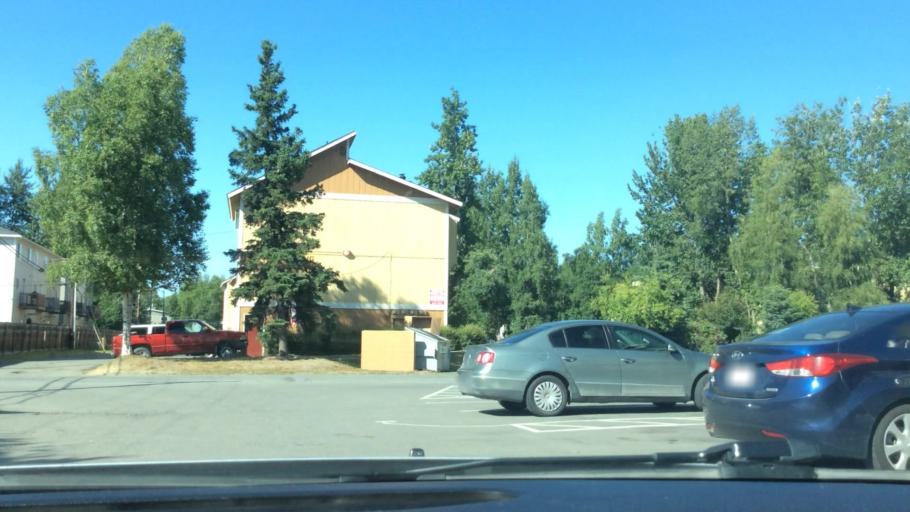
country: US
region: Alaska
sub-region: Anchorage Municipality
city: Anchorage
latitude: 61.1968
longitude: -149.7819
